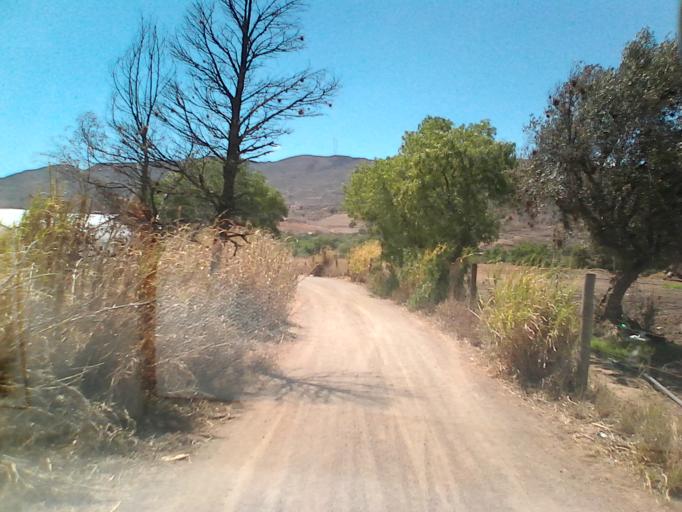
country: CO
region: Boyaca
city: Sachica
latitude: 5.6081
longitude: -73.5627
